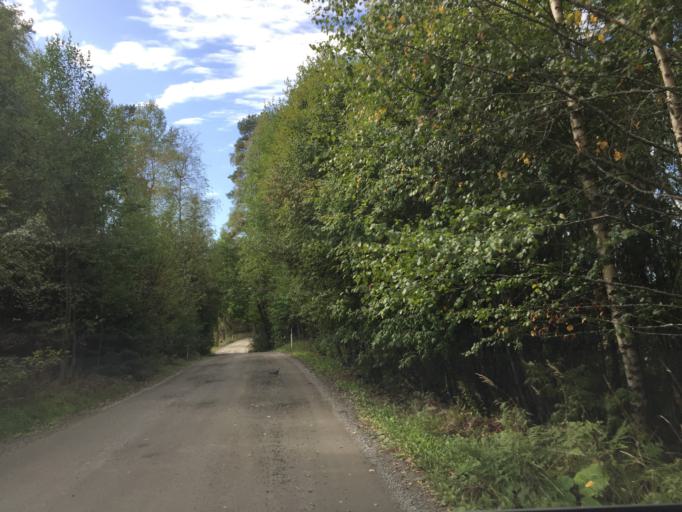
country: NO
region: Ostfold
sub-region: Hobol
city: Elvestad
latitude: 59.6430
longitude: 10.8901
